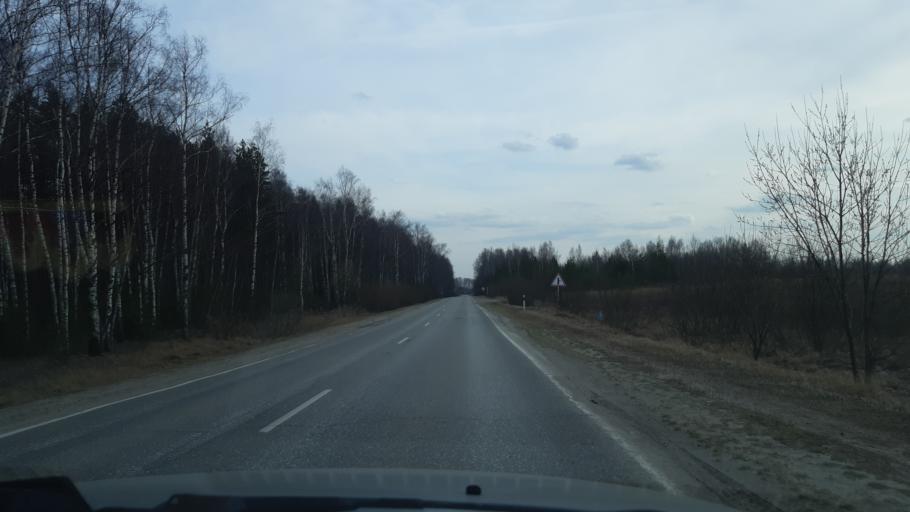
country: RU
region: Vladimir
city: Luknovo
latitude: 56.2307
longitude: 42.0345
